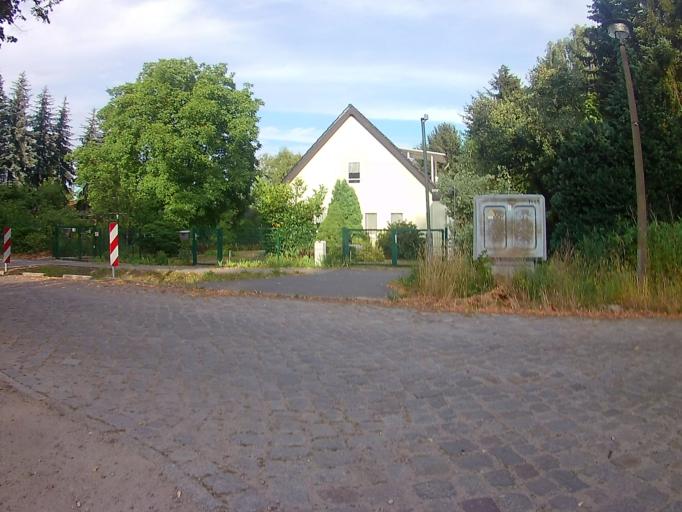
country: DE
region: Berlin
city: Adlershof
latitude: 52.4188
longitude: 13.5521
